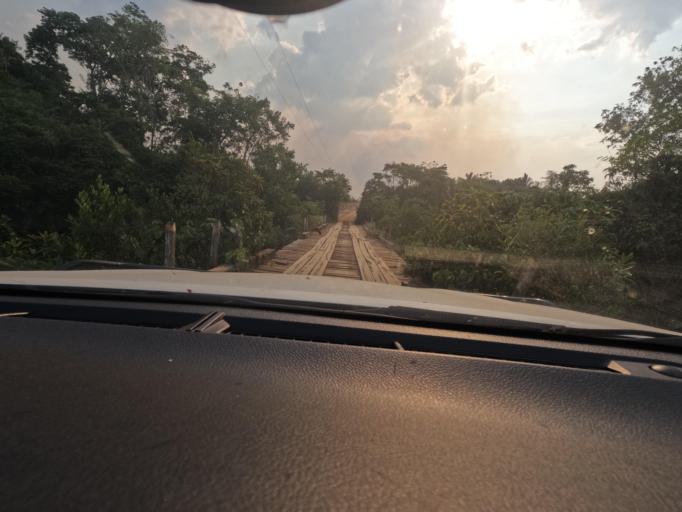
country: BR
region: Rondonia
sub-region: Porto Velho
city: Porto Velho
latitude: -8.6382
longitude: -63.1713
